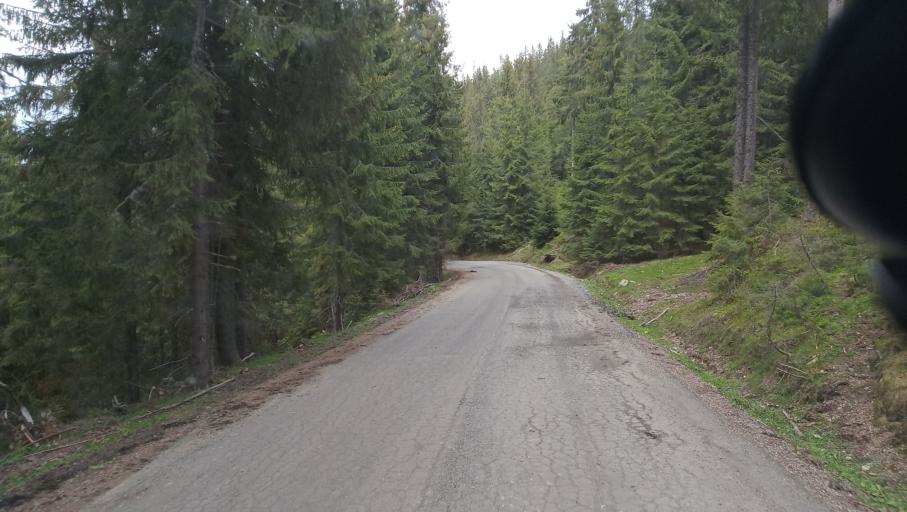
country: RO
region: Alba
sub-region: Comuna Horea
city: Horea
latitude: 46.5429
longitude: 22.8986
